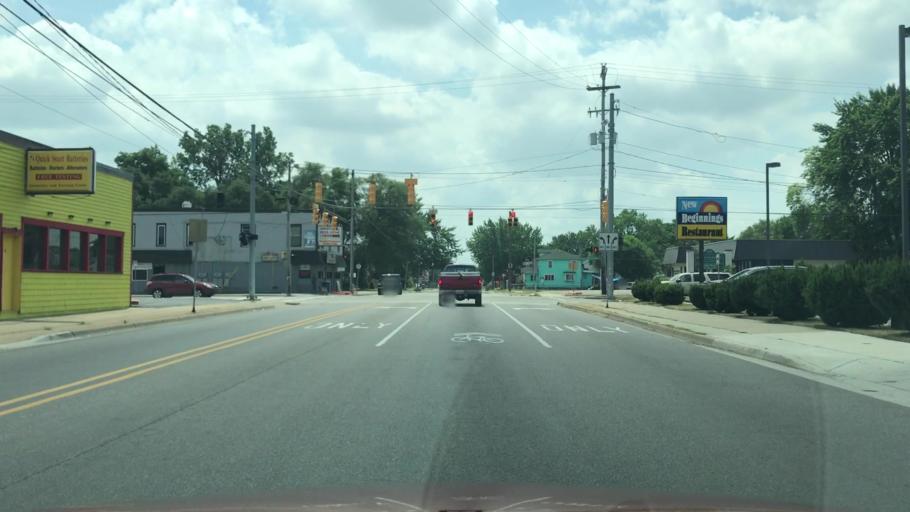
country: US
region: Michigan
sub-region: Kent County
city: Grand Rapids
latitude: 42.9930
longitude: -85.6883
